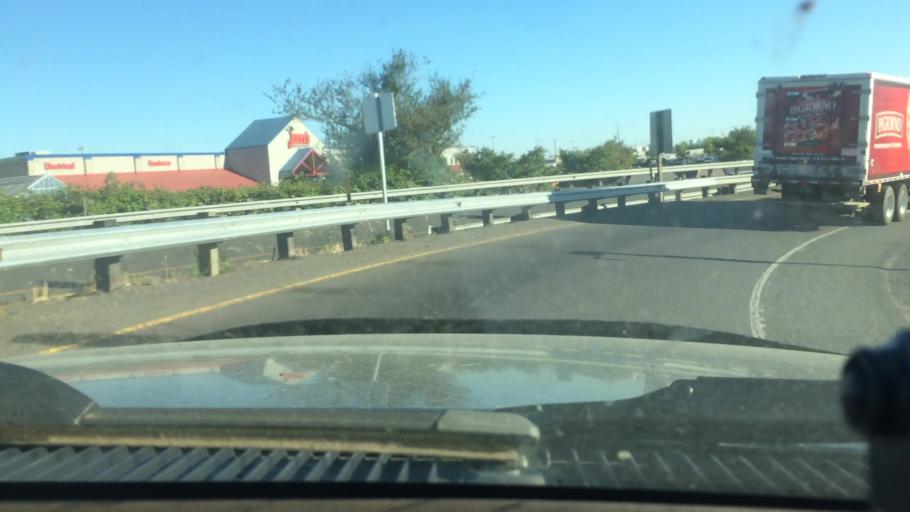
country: US
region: Oregon
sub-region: Lane County
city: Eugene
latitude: 44.0964
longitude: -123.1688
